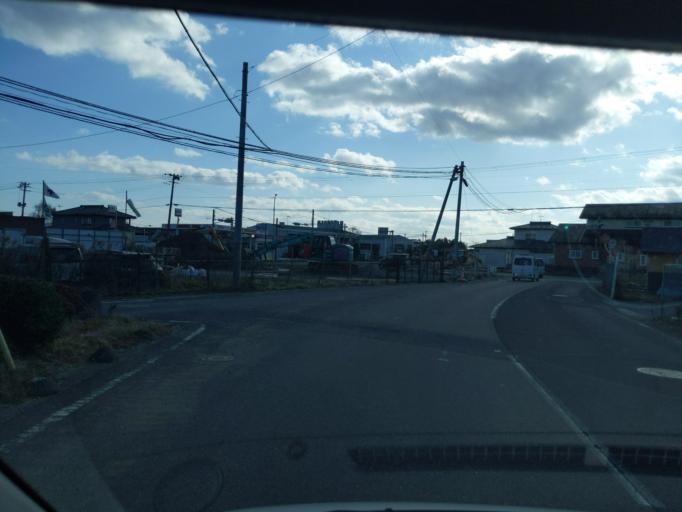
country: JP
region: Iwate
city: Ichinoseki
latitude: 38.7549
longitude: 141.0656
